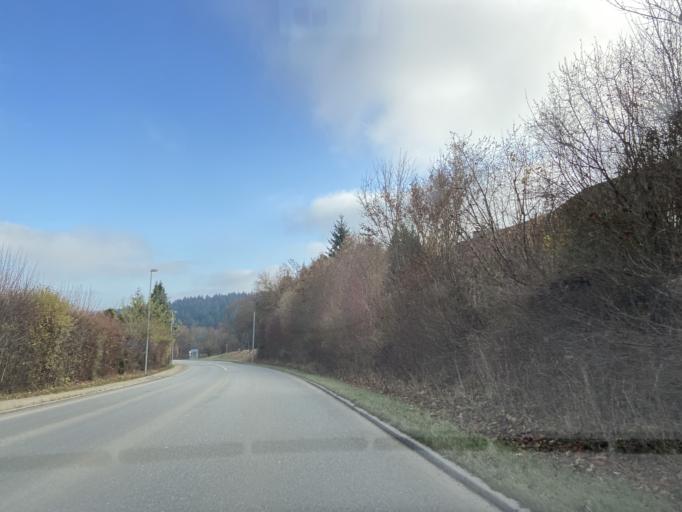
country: DE
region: Baden-Wuerttemberg
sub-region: Tuebingen Region
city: Gammertingen
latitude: 48.2429
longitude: 9.2074
